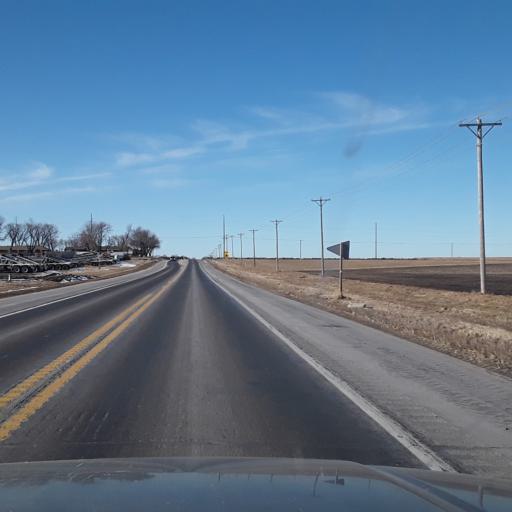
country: US
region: Nebraska
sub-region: Adams County
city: Hastings
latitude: 40.5680
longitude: -98.4162
